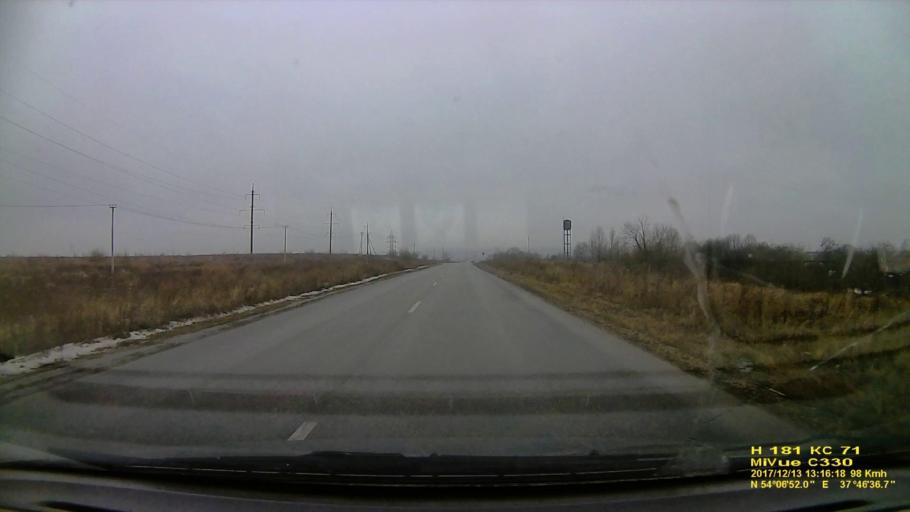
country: RU
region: Tula
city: Bolokhovo
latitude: 54.1145
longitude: 37.7764
